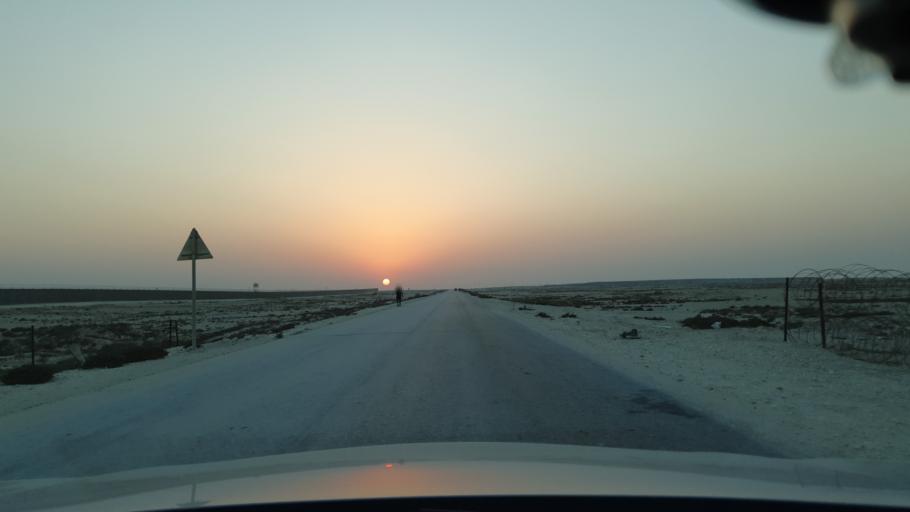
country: BH
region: Central Governorate
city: Dar Kulayb
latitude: 25.9557
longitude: 50.6096
